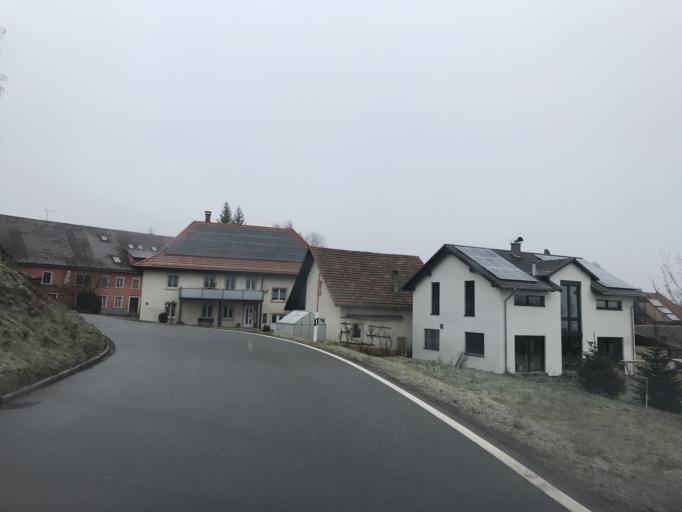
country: DE
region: Baden-Wuerttemberg
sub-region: Freiburg Region
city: Rickenbach
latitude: 47.6118
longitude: 7.9576
